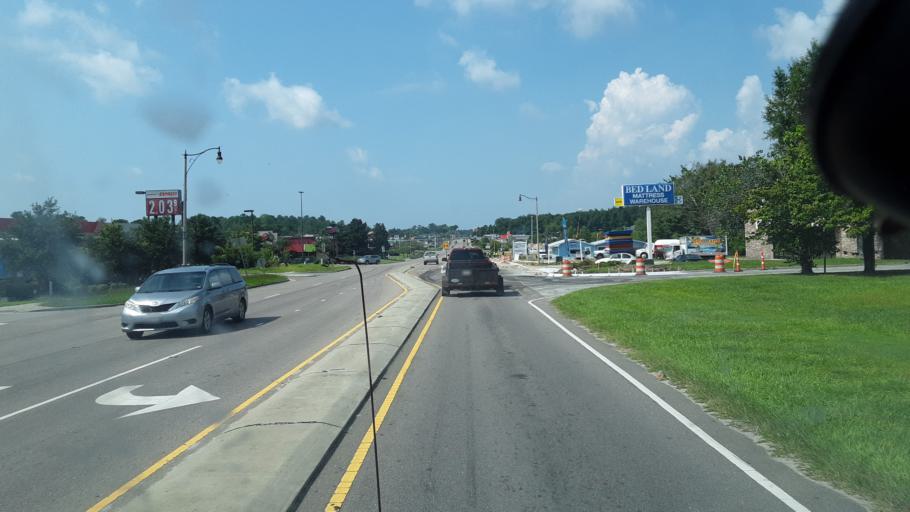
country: US
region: North Carolina
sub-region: Brunswick County
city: Shallotte
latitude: 33.9813
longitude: -78.3738
